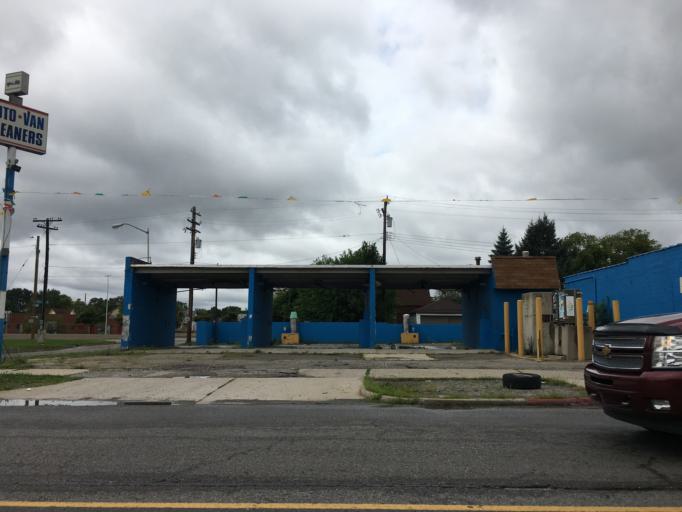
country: US
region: Michigan
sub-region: Oakland County
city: Oak Park
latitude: 42.4063
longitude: -83.1598
